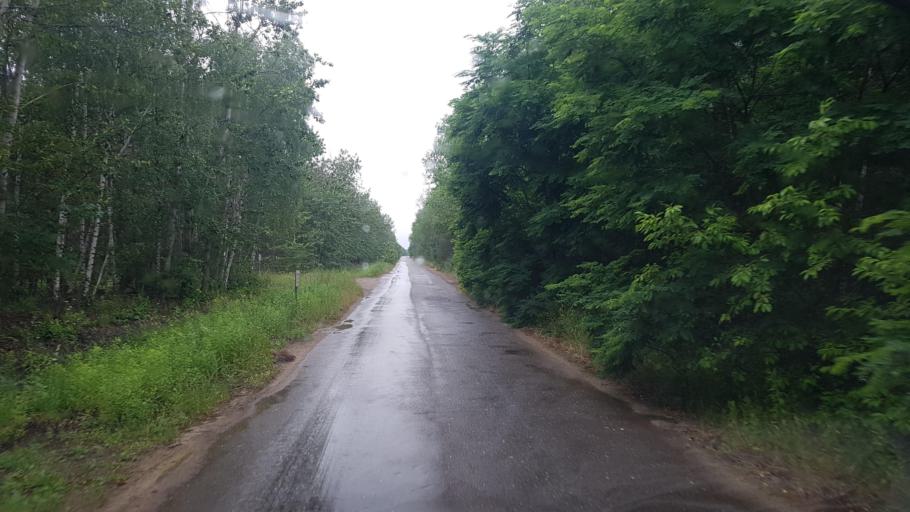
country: DE
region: Brandenburg
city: Lauchhammer
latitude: 51.5386
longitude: 13.7592
